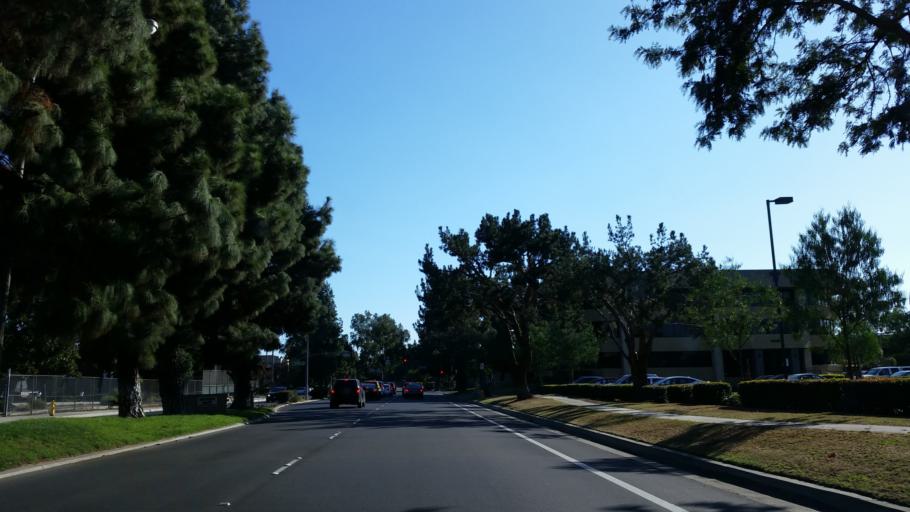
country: US
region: California
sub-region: Los Angeles County
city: Bellflower
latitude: 33.8742
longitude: -118.0999
